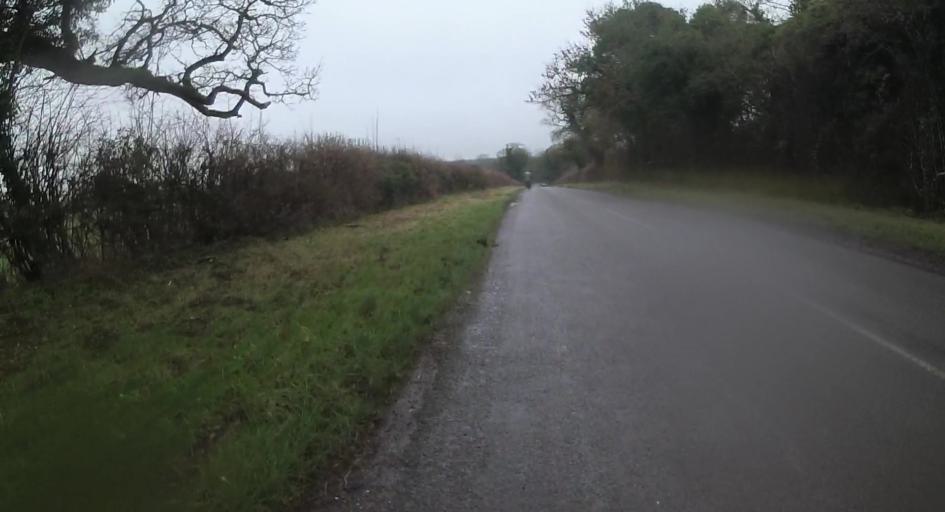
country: GB
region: England
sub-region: Hampshire
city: Kings Worthy
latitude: 51.1266
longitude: -1.2252
